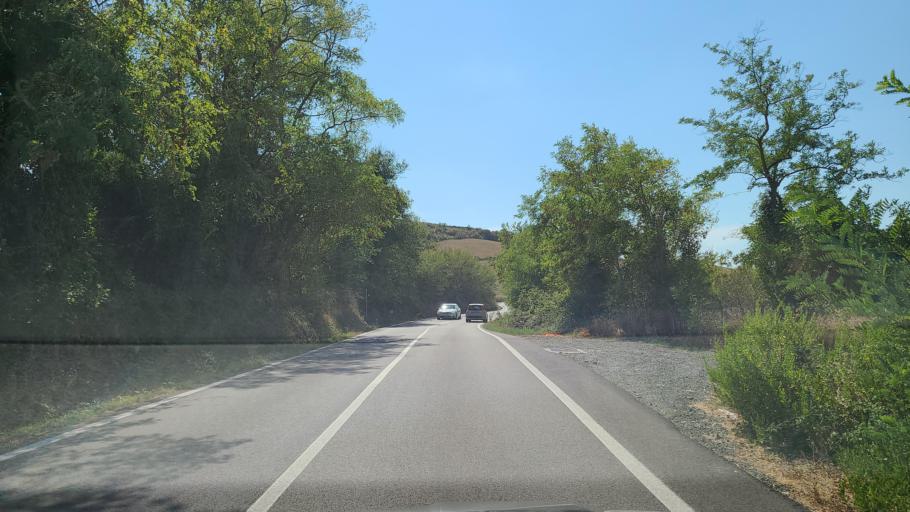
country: IT
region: Tuscany
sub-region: Province of Pisa
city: Volterra
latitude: 43.3865
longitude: 10.9122
